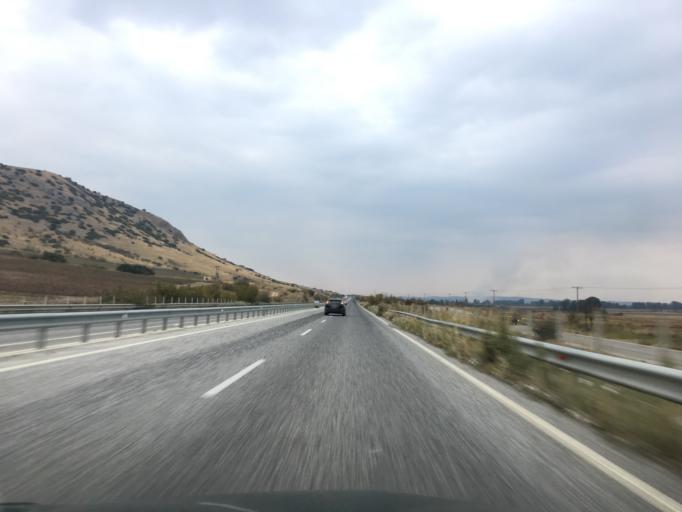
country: GR
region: Thessaly
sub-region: Trikala
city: Zarkos
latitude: 39.5965
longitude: 22.1876
